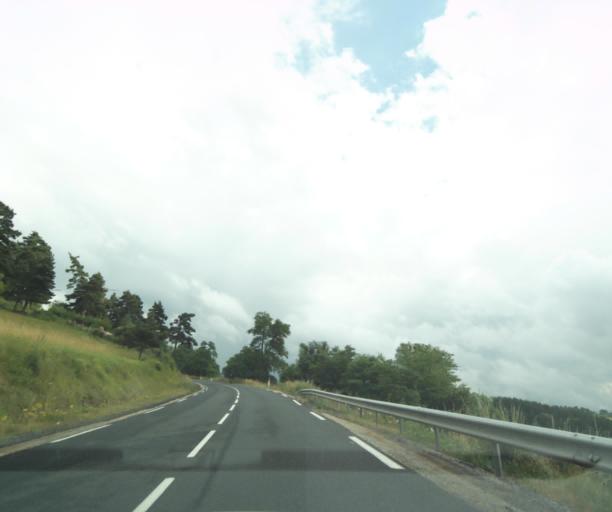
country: FR
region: Auvergne
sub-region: Departement de la Haute-Loire
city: Bains
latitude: 44.9957
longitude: 3.6904
